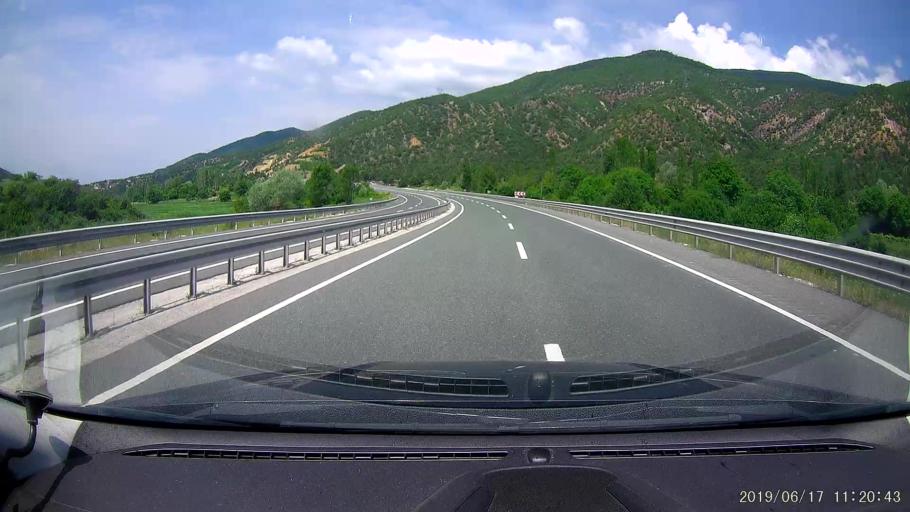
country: TR
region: Cankiri
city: Yaprakli
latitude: 40.9122
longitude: 33.7998
